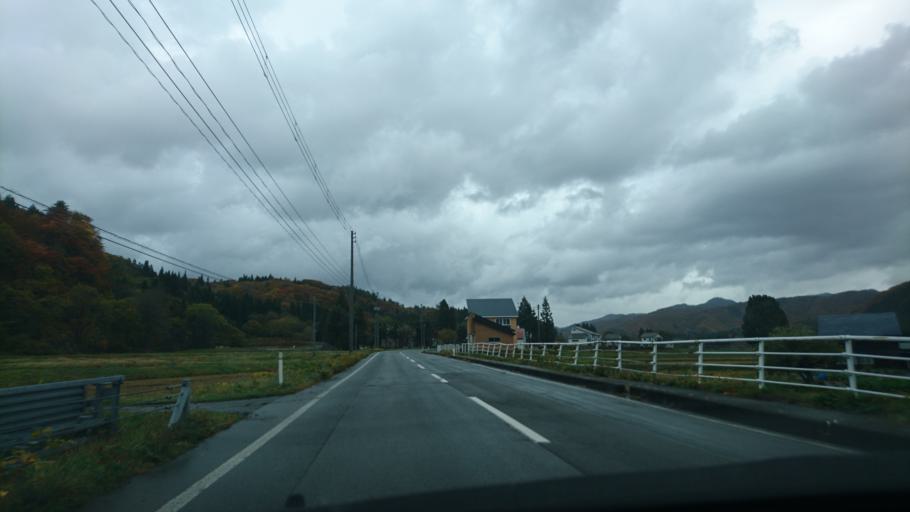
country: JP
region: Akita
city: Kakunodatemachi
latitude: 39.4867
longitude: 140.8062
